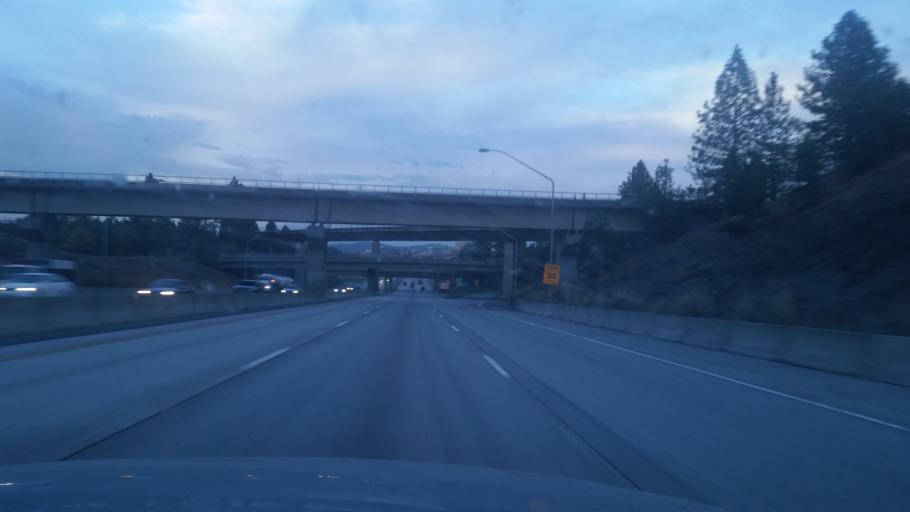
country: US
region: Washington
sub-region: Spokane County
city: Spokane
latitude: 47.6451
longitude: -117.4548
